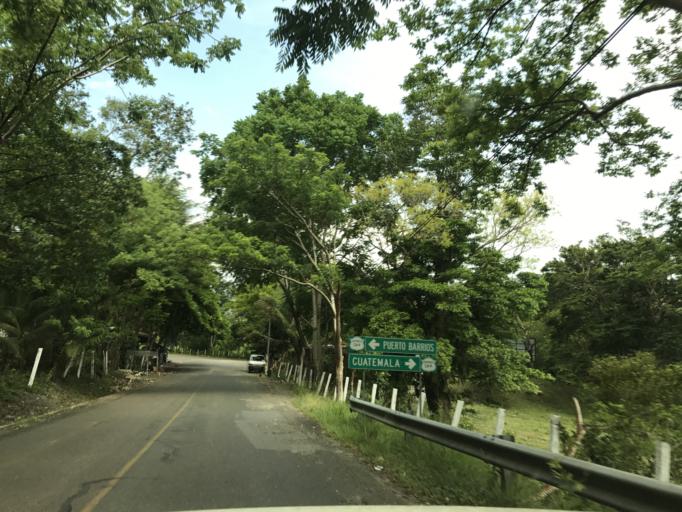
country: GT
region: Izabal
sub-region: Municipio de Los Amates
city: Los Amates
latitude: 15.3798
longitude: -89.0217
